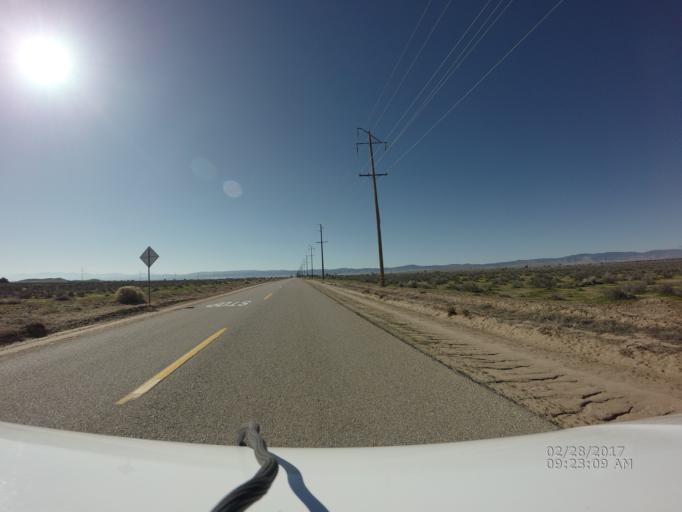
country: US
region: California
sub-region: Kern County
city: Rosamond
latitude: 34.8178
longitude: -118.3261
